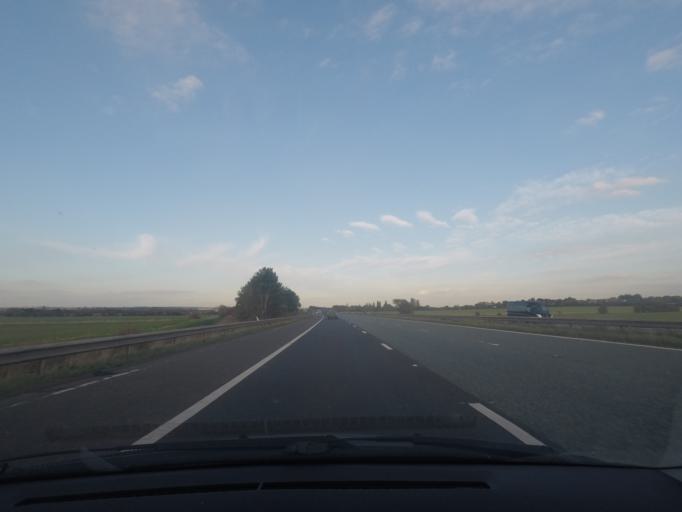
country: GB
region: England
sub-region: North Lincolnshire
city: Brigg
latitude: 53.5662
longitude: -0.4810
